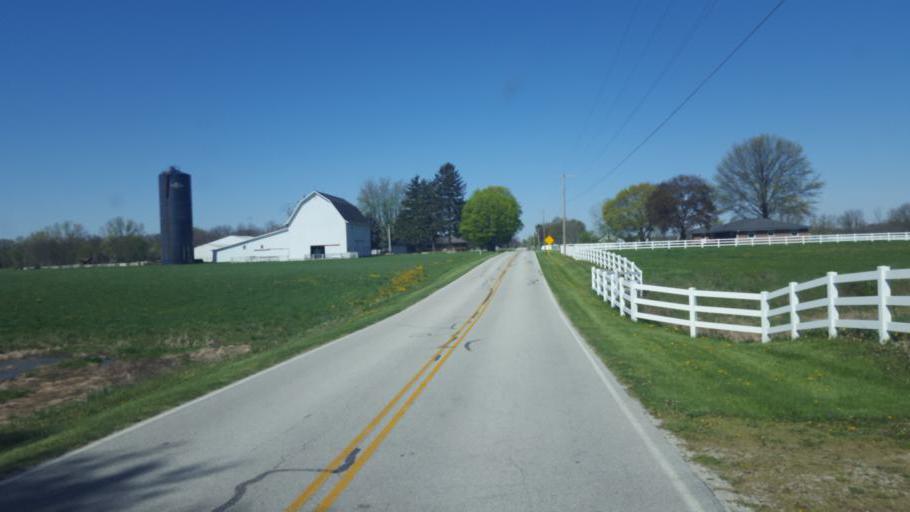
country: US
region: Ohio
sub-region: Seneca County
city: Tiffin
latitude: 41.2113
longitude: -83.1772
